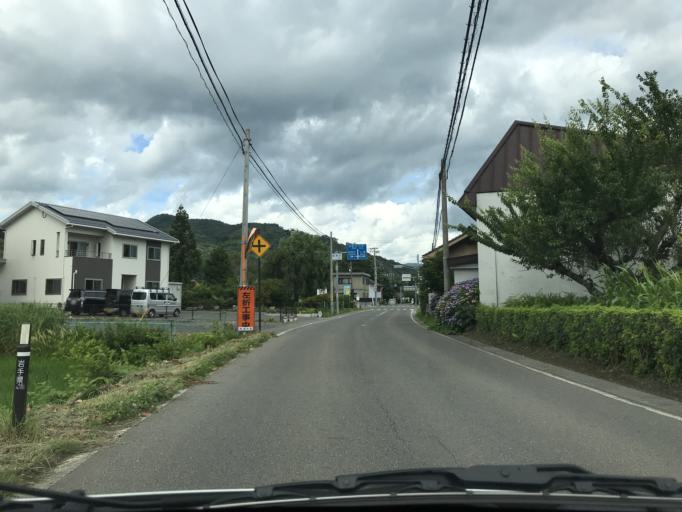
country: JP
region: Iwate
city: Tono
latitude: 39.3558
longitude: 141.5666
